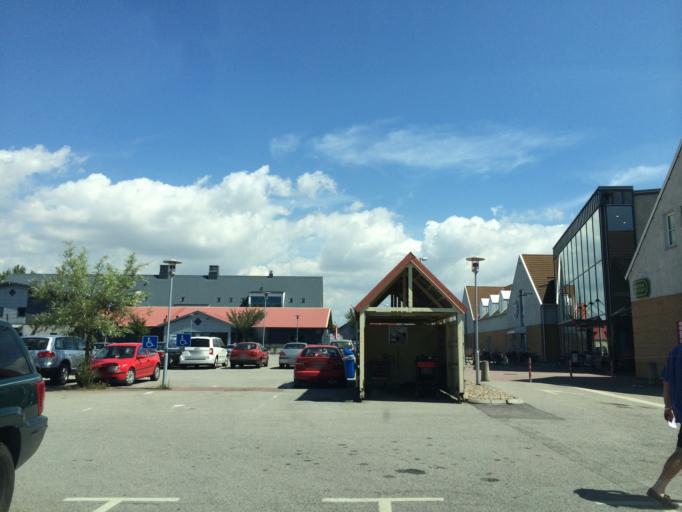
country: SE
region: Skane
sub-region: Vellinge Kommun
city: Hollviken
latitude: 55.4262
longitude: 12.9640
